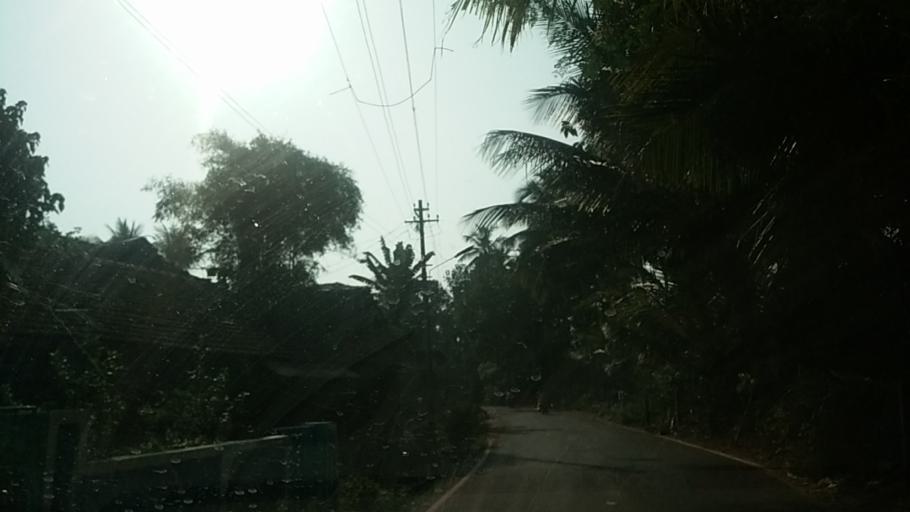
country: IN
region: Goa
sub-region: North Goa
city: Pernem
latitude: 15.7322
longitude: 73.7599
